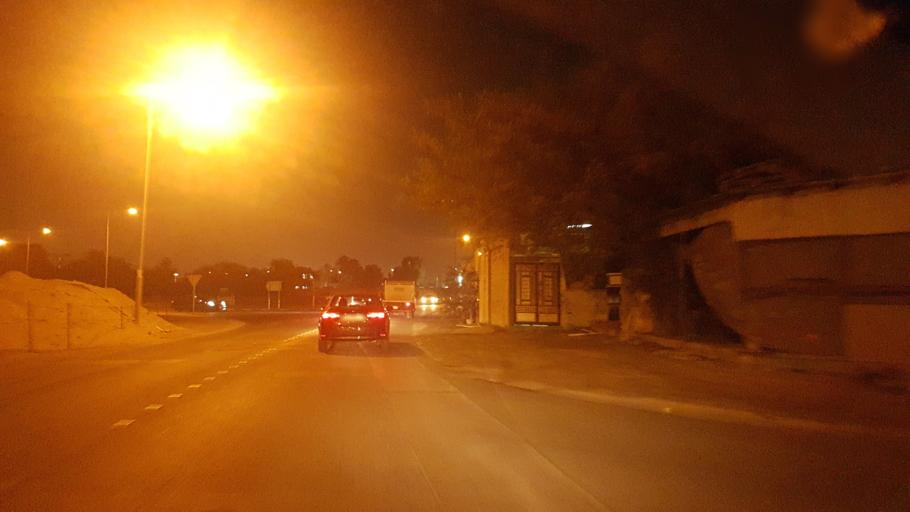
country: BH
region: Manama
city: Jidd Hafs
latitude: 26.2264
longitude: 50.5191
